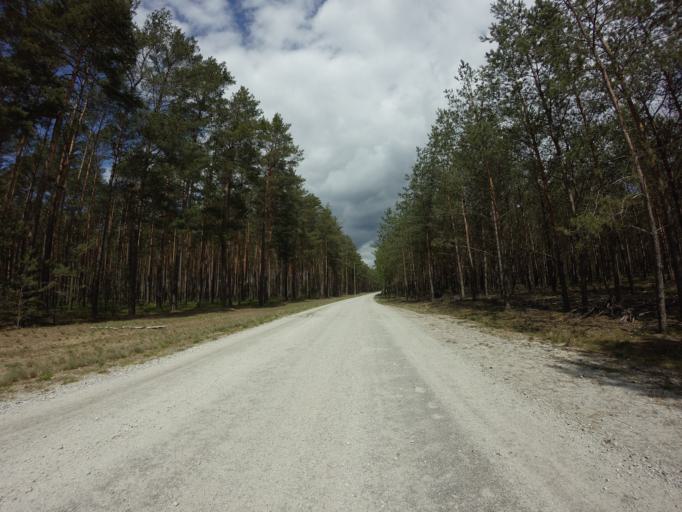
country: PL
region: West Pomeranian Voivodeship
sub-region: Powiat drawski
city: Kalisz Pomorski
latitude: 53.1874
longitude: 15.9730
